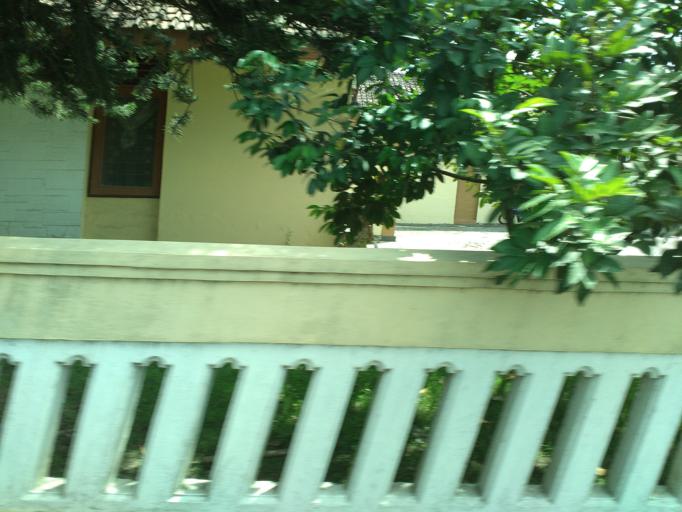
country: ID
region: Central Java
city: Kebonarun
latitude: -7.7178
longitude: 110.5781
